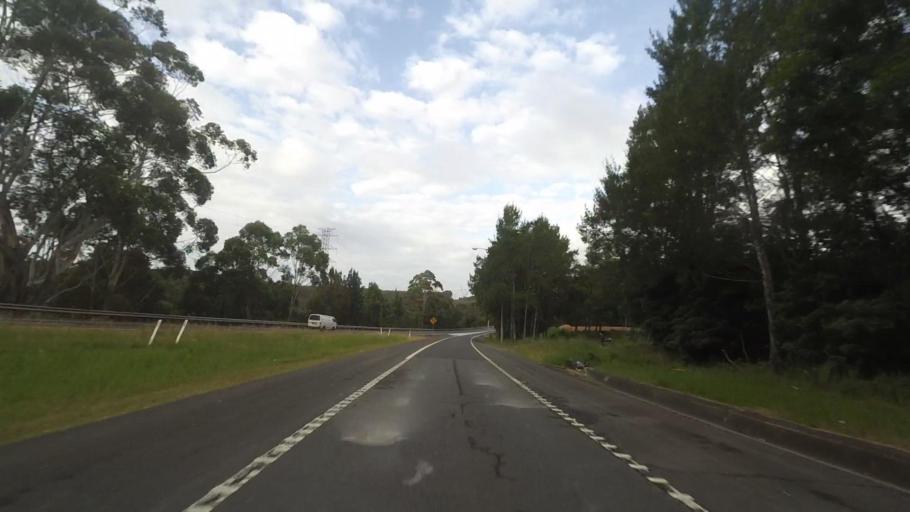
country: AU
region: New South Wales
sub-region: Wollongong
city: Bulli
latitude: -34.3086
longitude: 150.8985
